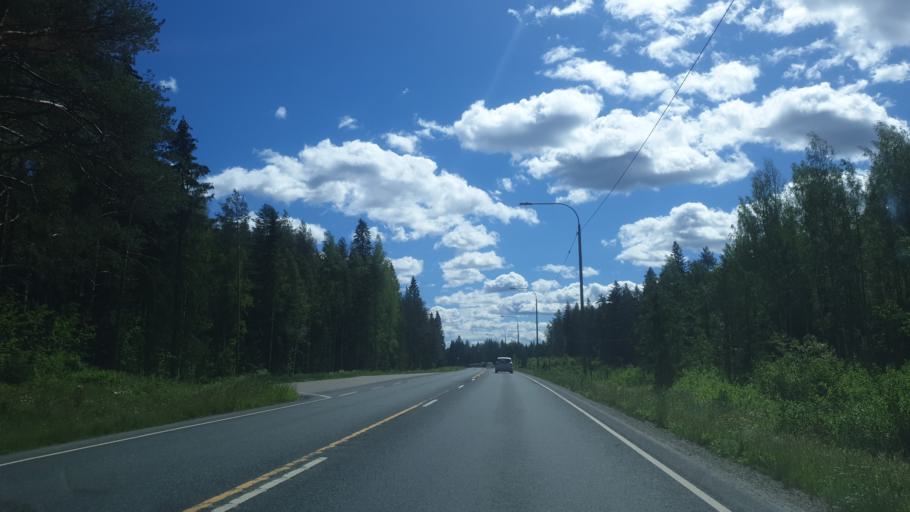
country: FI
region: Northern Savo
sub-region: Varkaus
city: Leppaevirta
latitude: 62.5286
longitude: 27.6607
